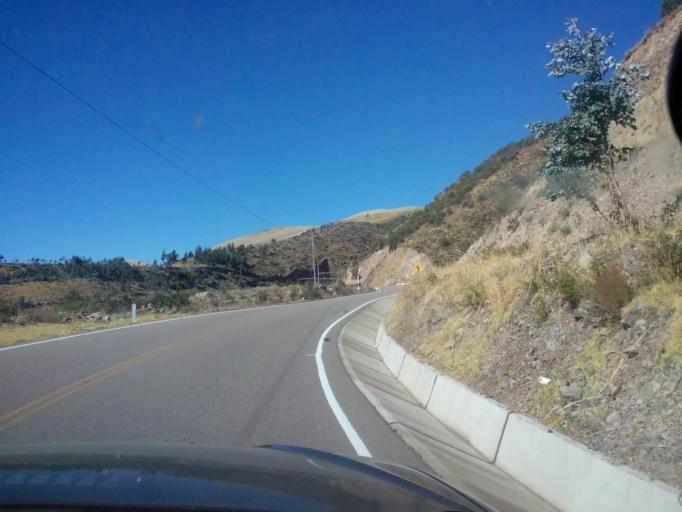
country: PE
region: Ayacucho
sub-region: Provincia de Huamanga
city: Chiara
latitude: -13.2849
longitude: -74.2303
